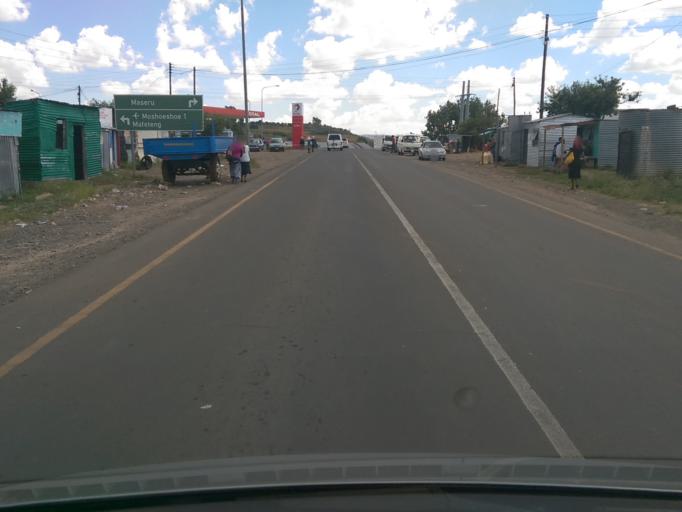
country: LS
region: Maseru
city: Maseru
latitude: -29.4038
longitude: 27.5627
